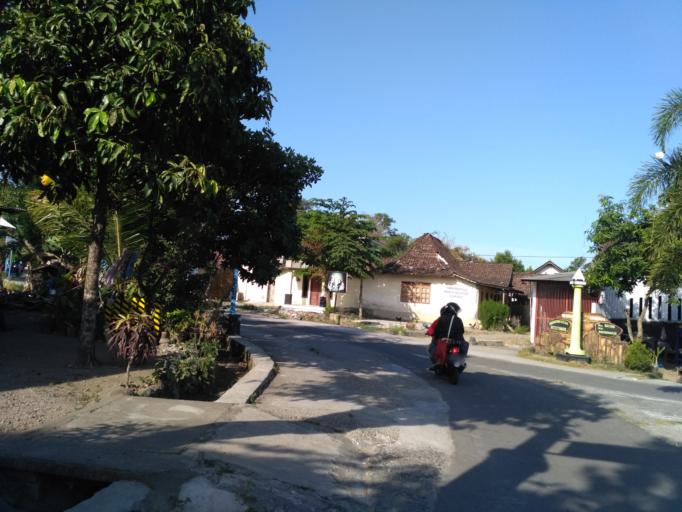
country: ID
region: Daerah Istimewa Yogyakarta
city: Depok
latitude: -7.7743
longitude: 110.4271
